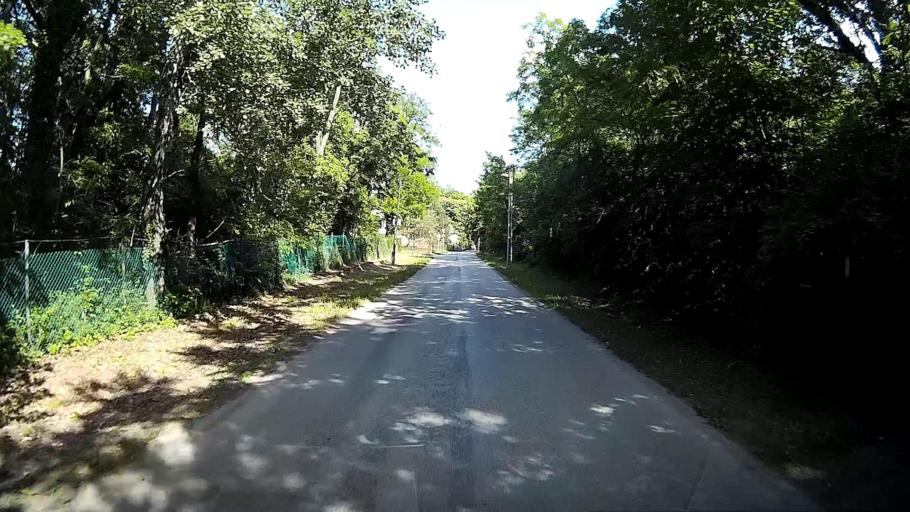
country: HU
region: Pest
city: God
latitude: 47.6616
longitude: 19.1095
